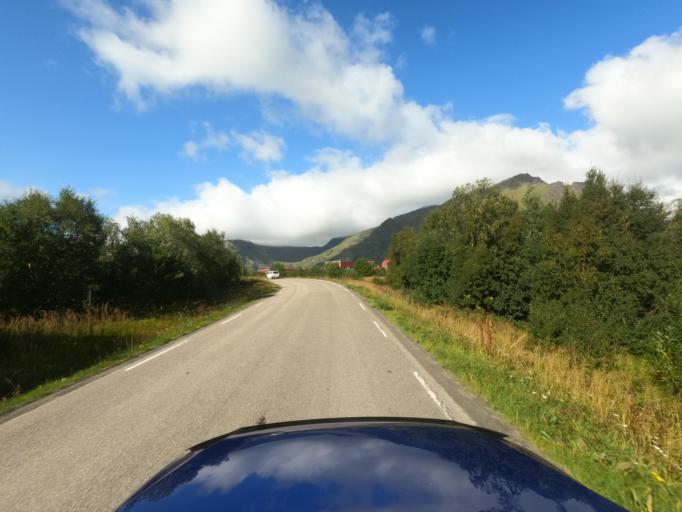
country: NO
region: Nordland
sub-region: Vestvagoy
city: Evjen
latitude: 68.1534
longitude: 13.8332
